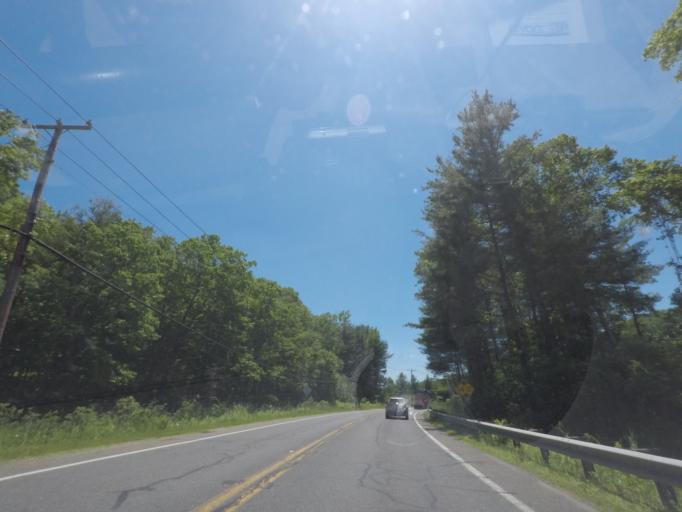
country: US
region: Massachusetts
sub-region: Berkshire County
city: Becket
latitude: 42.2790
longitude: -73.1417
